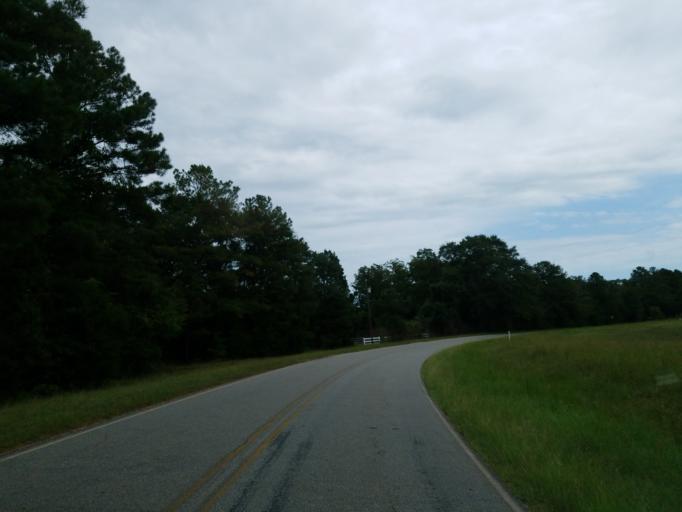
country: US
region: Georgia
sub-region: Monroe County
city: Forsyth
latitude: 32.9494
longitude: -83.9483
